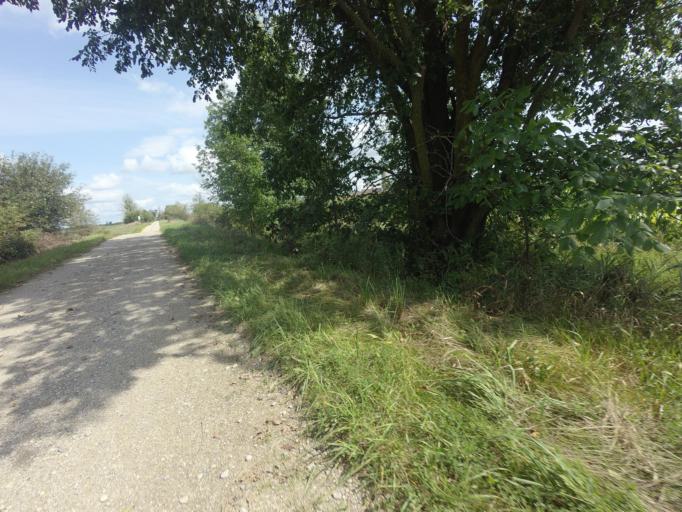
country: CA
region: Ontario
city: Waterloo
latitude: 43.5884
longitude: -80.7015
